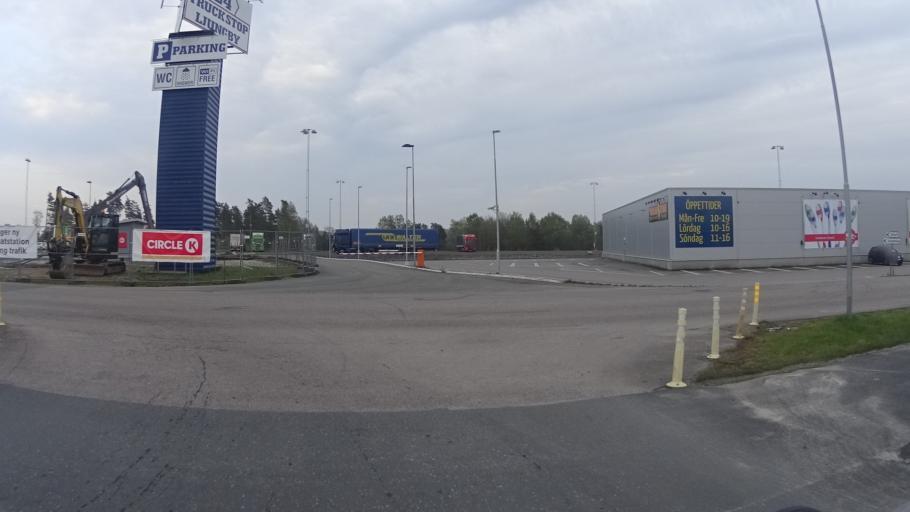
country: SE
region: Kronoberg
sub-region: Ljungby Kommun
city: Ljungby
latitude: 56.8120
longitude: 13.9091
